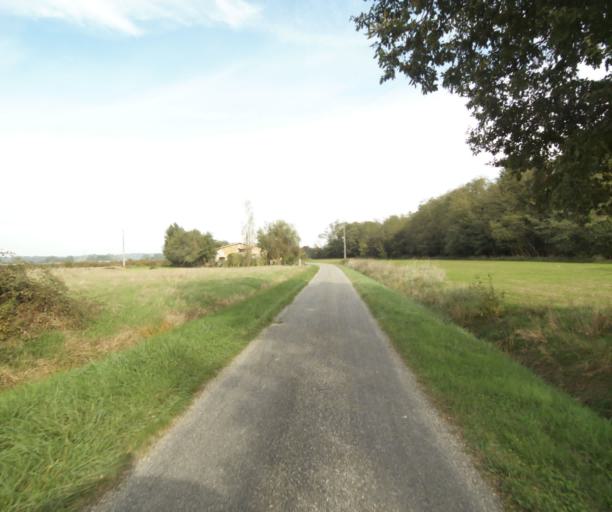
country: FR
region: Midi-Pyrenees
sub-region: Departement du Tarn-et-Garonne
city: Labastide-Saint-Pierre
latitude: 43.9279
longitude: 1.3502
